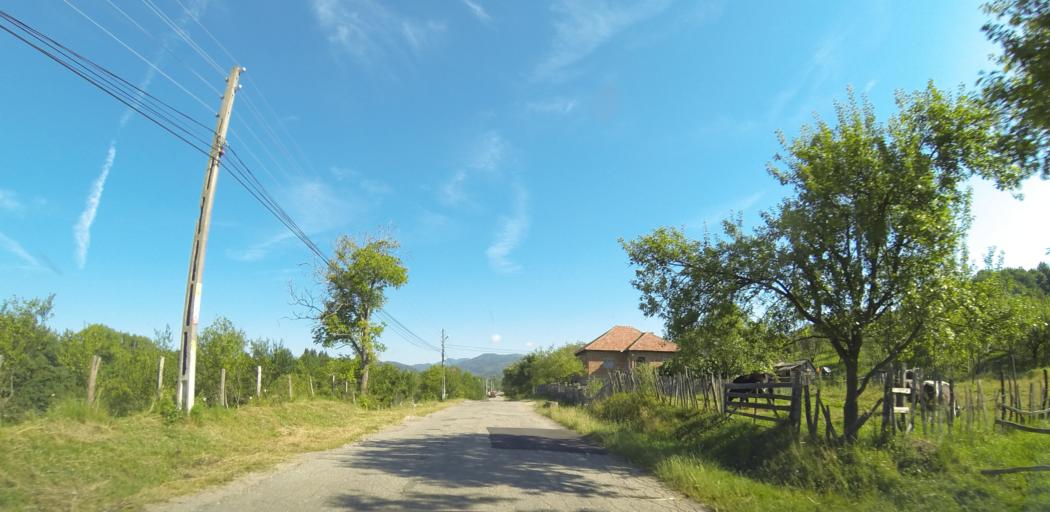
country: RO
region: Valcea
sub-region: Comuna Slatioara
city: Slatioara
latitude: 45.1560
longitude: 23.8669
